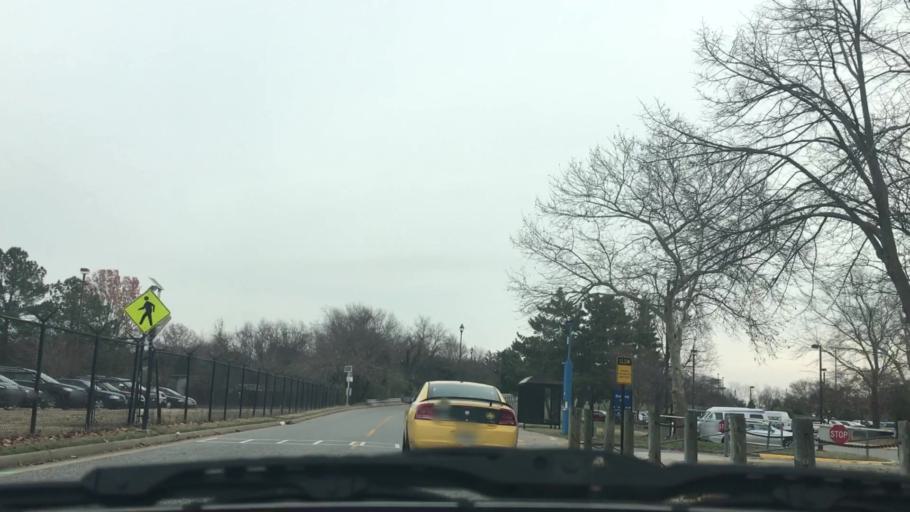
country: US
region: Virginia
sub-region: City of Hampton
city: Hampton
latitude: 37.0175
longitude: -76.3298
